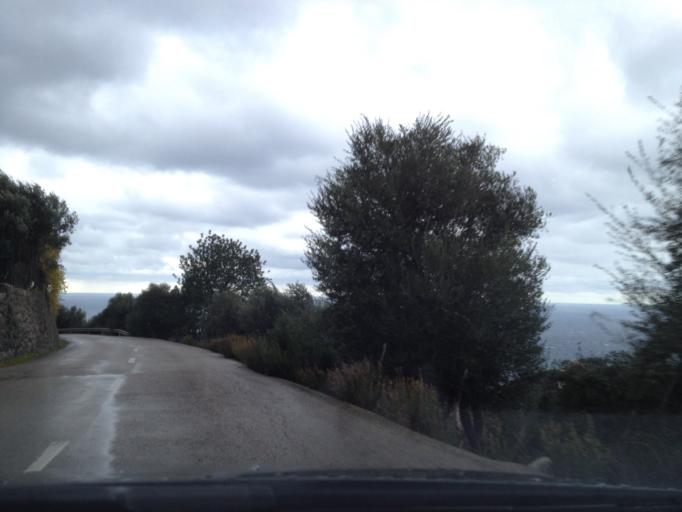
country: ES
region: Balearic Islands
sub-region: Illes Balears
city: Deia
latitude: 39.7746
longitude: 2.6742
